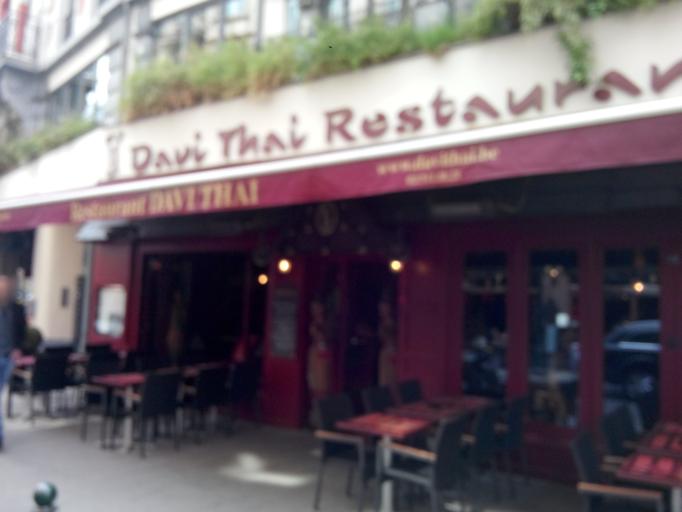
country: BE
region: Brussels Capital
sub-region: Bruxelles-Capitale
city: Brussels
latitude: 50.8483
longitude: 4.3483
